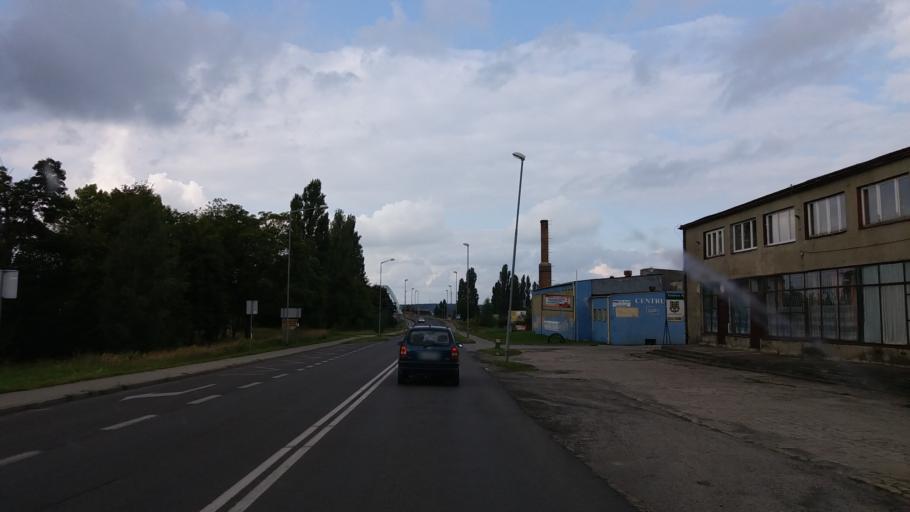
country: PL
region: West Pomeranian Voivodeship
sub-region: Powiat choszczenski
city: Choszczno
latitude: 53.1632
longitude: 15.4000
